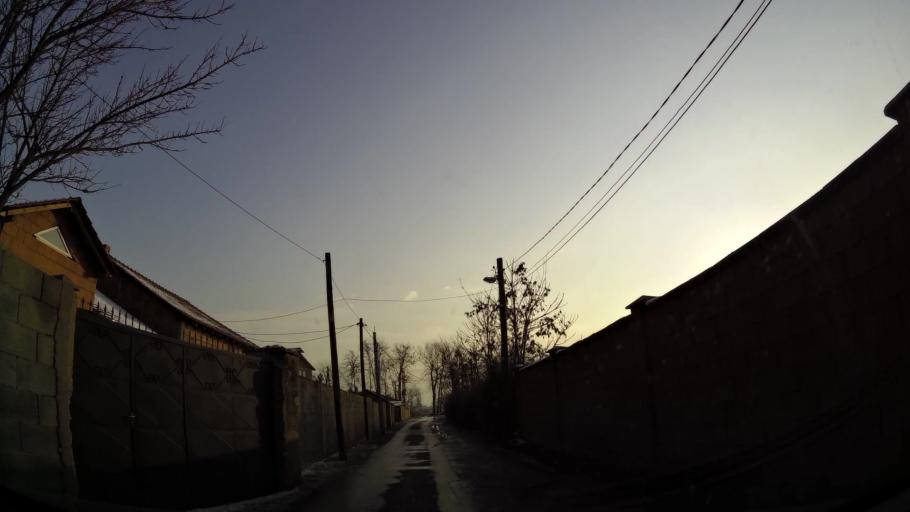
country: MK
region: Aracinovo
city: Arachinovo
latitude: 42.0142
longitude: 21.5260
